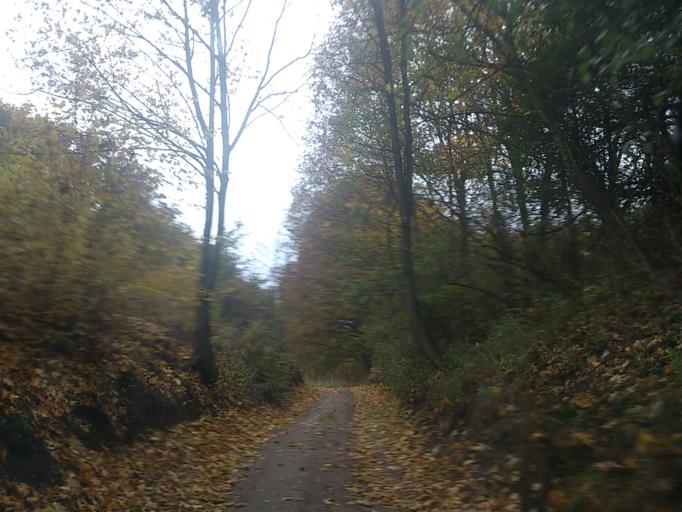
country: PL
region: Kujawsko-Pomorskie
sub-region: Powiat golubsko-dobrzynski
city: Golub-Dobrzyn
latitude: 53.1207
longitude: 19.0679
